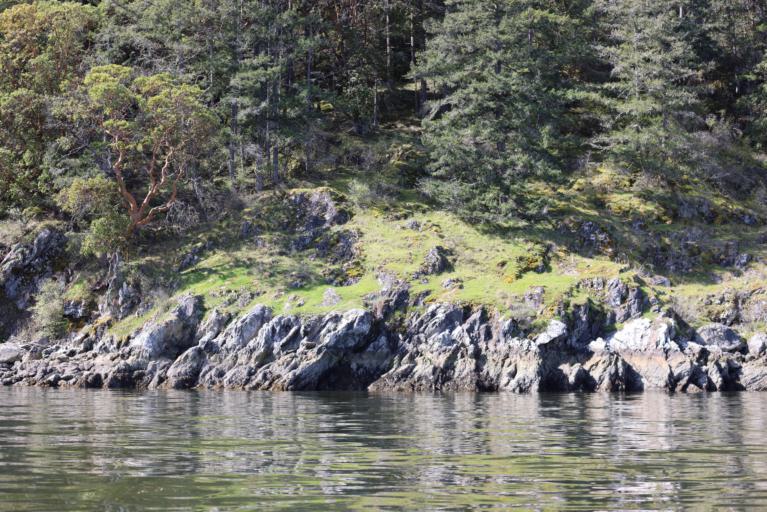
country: CA
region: British Columbia
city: Langford
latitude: 48.5738
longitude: -123.5151
